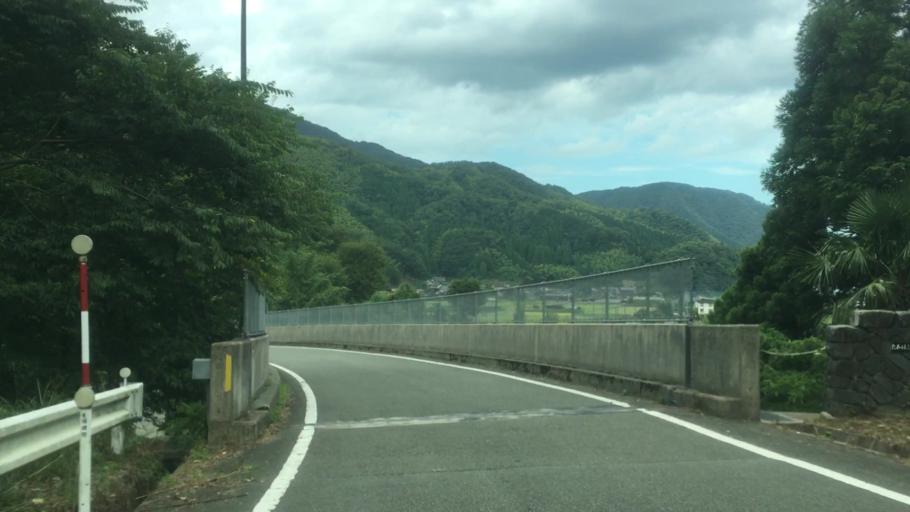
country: JP
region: Hyogo
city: Toyooka
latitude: 35.5861
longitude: 134.7993
